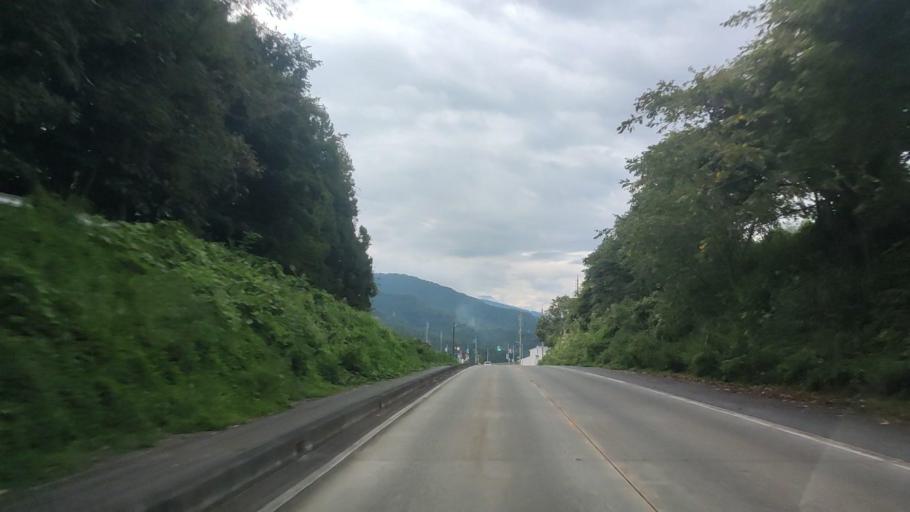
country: JP
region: Nagano
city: Iiyama
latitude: 36.8879
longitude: 138.4092
